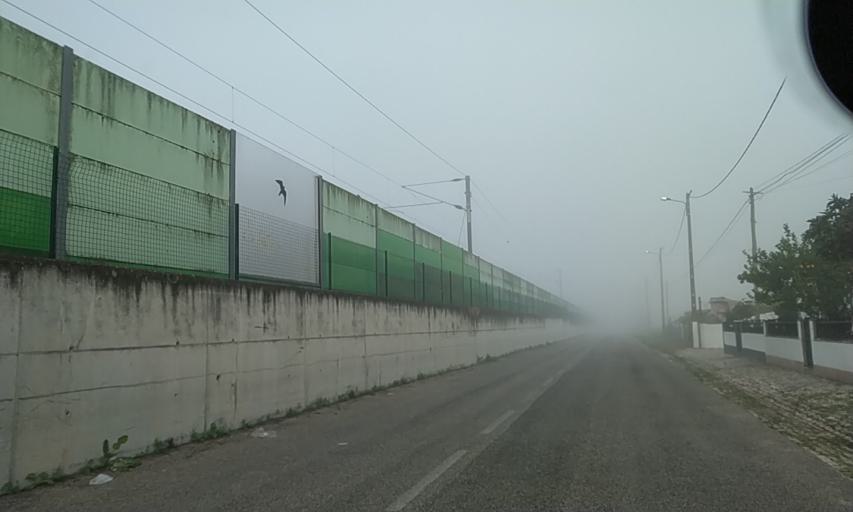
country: PT
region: Setubal
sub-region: Palmela
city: Pinhal Novo
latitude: 38.6118
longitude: -8.8925
